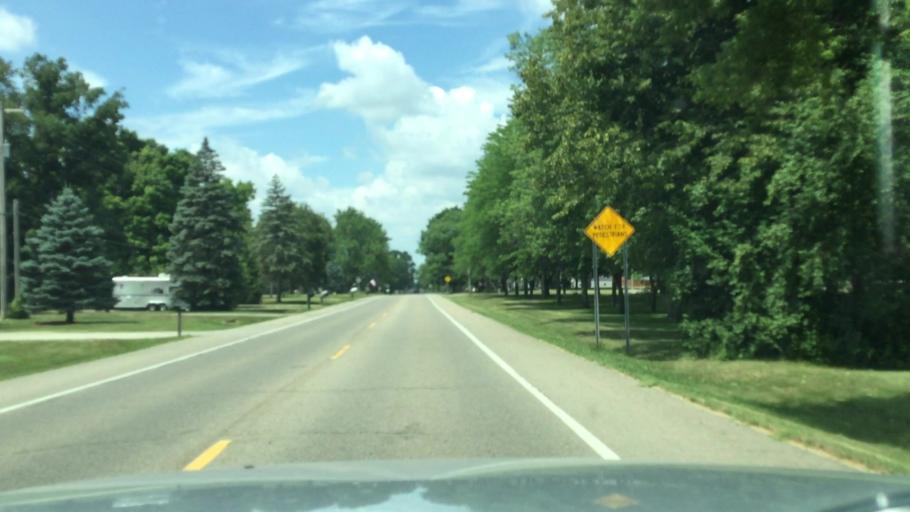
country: US
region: Michigan
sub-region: Genesee County
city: Flushing
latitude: 43.0674
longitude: -83.8155
